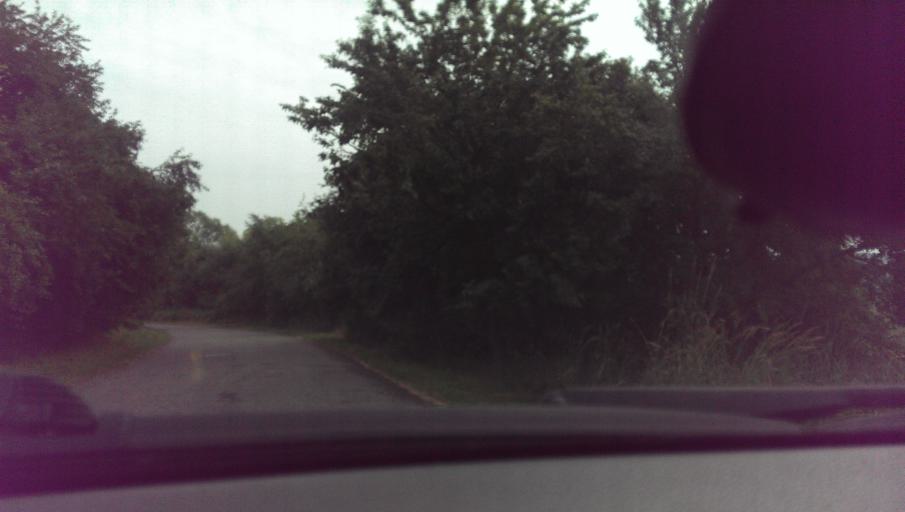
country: CZ
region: Zlin
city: Tecovice
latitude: 49.2139
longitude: 17.5777
